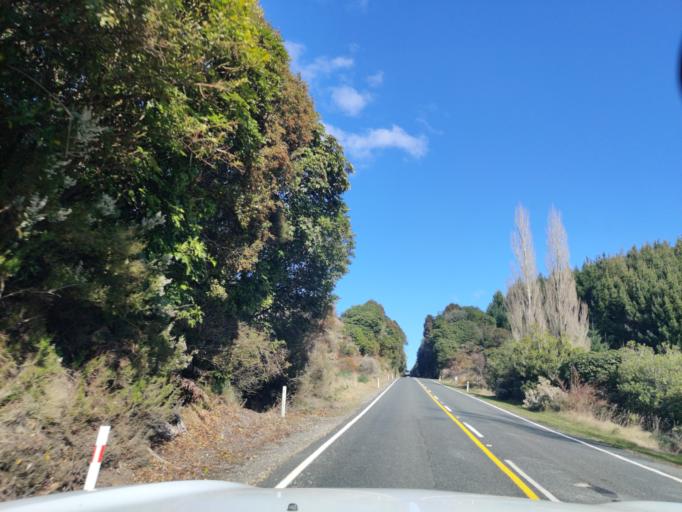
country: NZ
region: Waikato
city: Turangi
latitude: -38.7059
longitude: 175.6762
